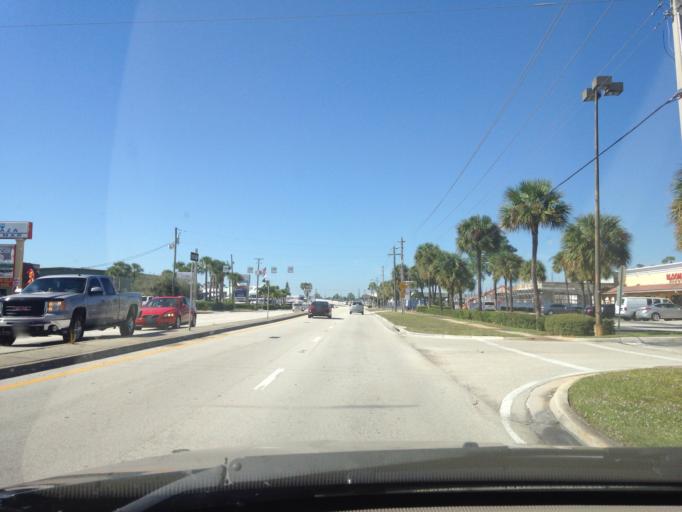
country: US
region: Florida
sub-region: Martin County
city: Palm City
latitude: 27.1758
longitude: -80.2538
